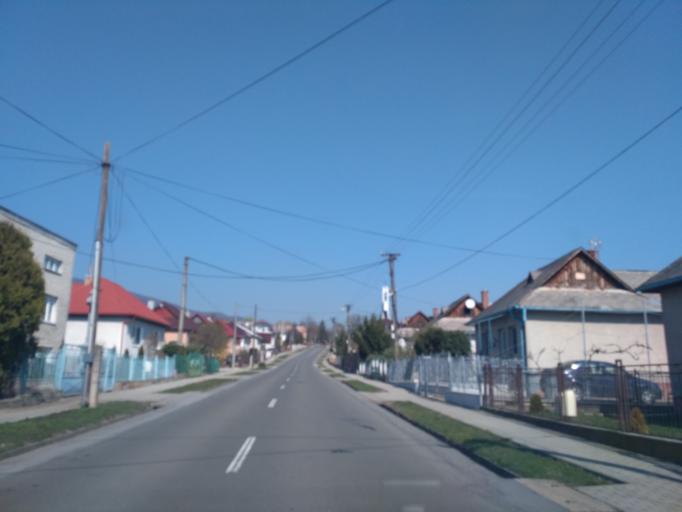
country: SK
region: Kosicky
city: Secovce
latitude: 48.7565
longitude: 21.6427
